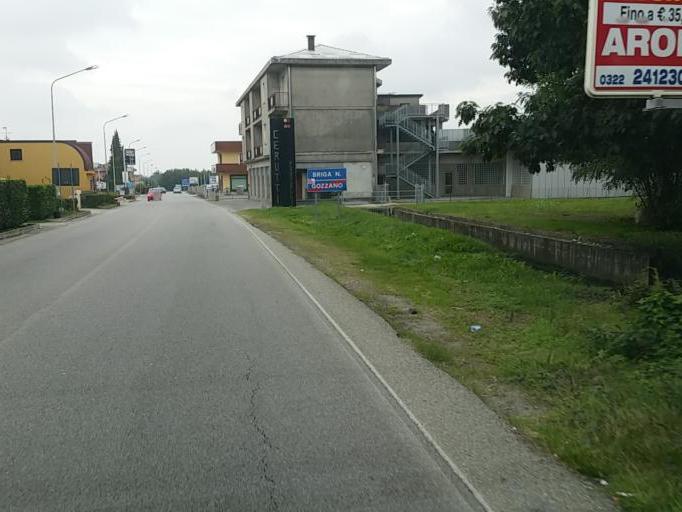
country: IT
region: Piedmont
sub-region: Provincia di Novara
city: Briga Novarese
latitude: 45.7282
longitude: 8.4442
